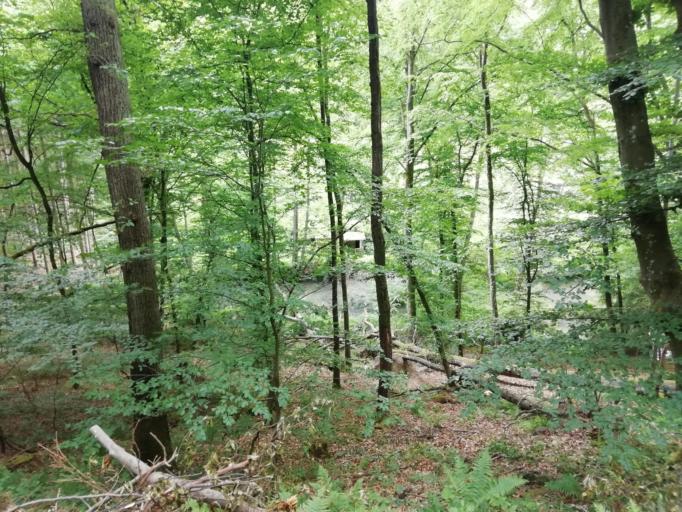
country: DE
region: Rheinland-Pfalz
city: Bad Neuenahr-Ahrweiler
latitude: 50.5098
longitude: 7.0948
